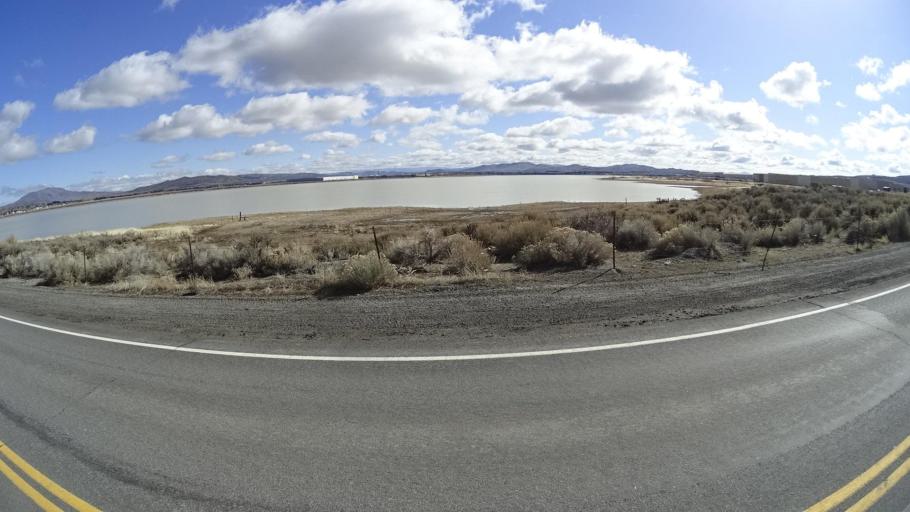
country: US
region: Nevada
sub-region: Washoe County
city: Cold Springs
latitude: 39.6413
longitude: -119.9254
